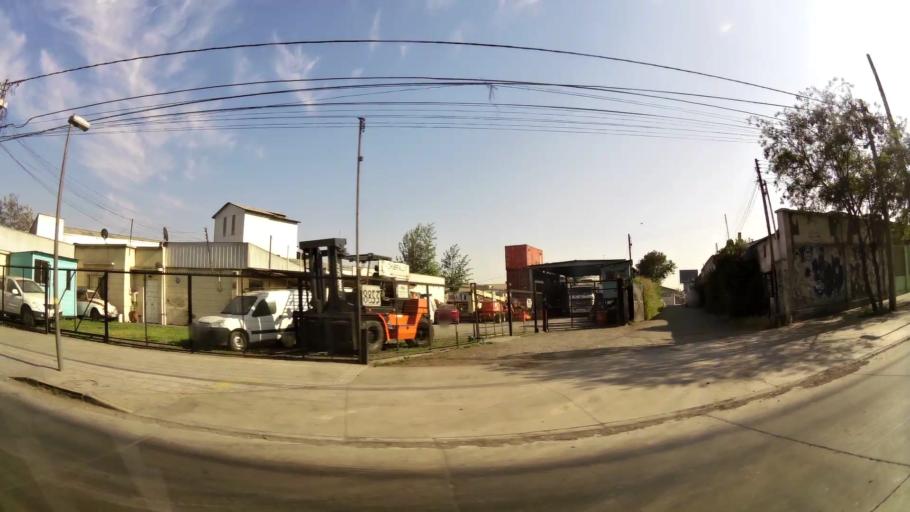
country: CL
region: Santiago Metropolitan
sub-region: Provincia de Santiago
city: Lo Prado
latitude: -33.5108
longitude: -70.7253
